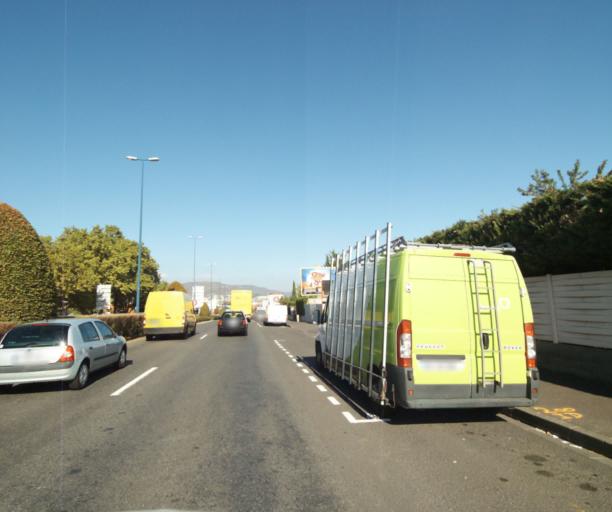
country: FR
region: Auvergne
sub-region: Departement du Puy-de-Dome
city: Aubiere
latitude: 45.7738
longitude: 3.1203
